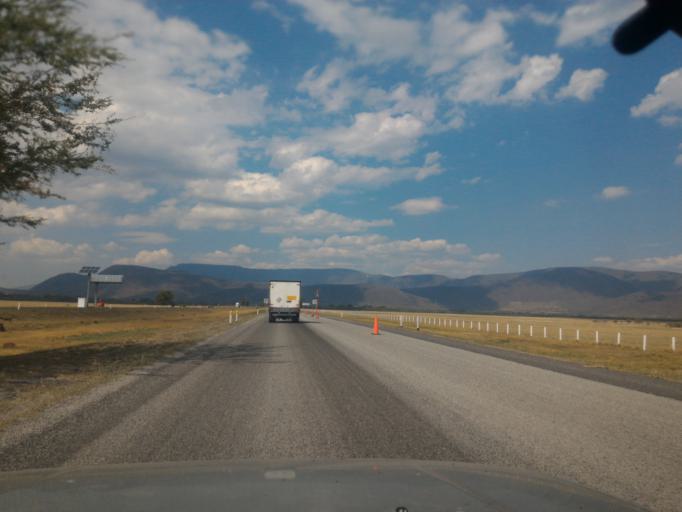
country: MX
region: Jalisco
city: Zacoalco de Torres
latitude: 20.1370
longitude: -103.5057
